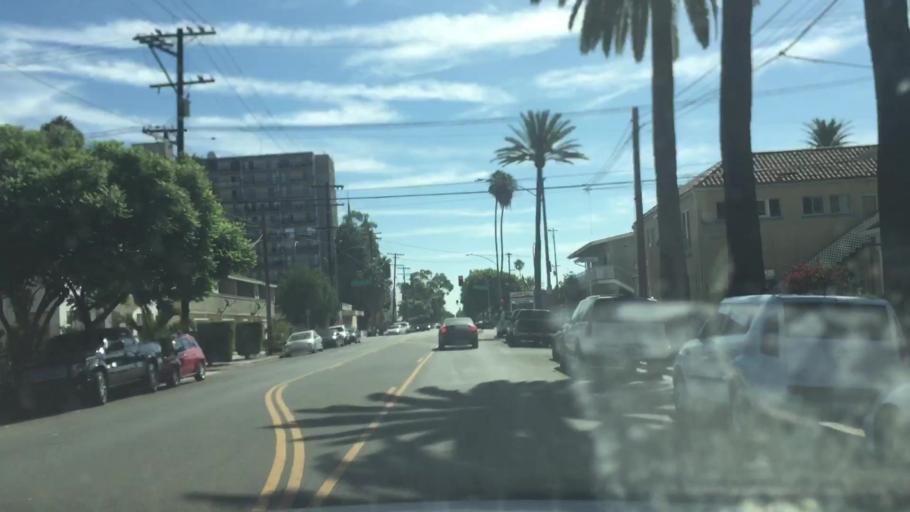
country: US
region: California
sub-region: Los Angeles County
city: Long Beach
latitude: 33.7789
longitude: -118.1948
